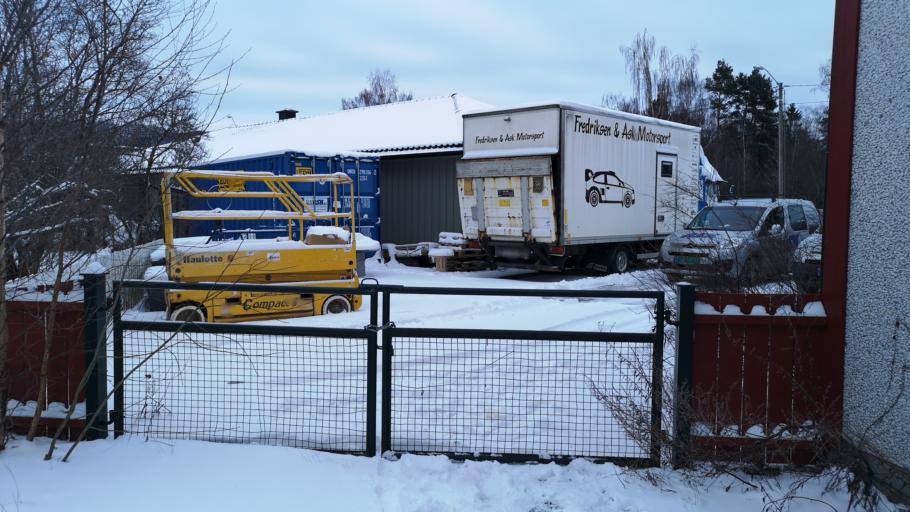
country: NO
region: Buskerud
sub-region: Ovre Eiker
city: Hokksund
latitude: 59.7694
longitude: 9.9125
